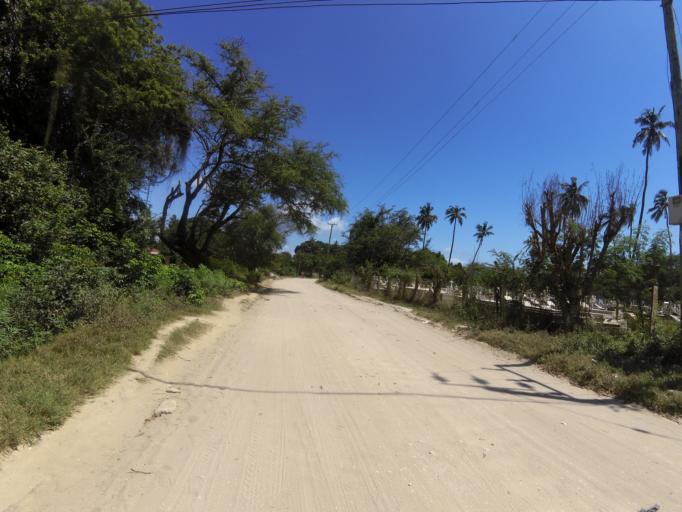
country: TZ
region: Dar es Salaam
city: Magomeni
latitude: -6.7926
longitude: 39.2725
